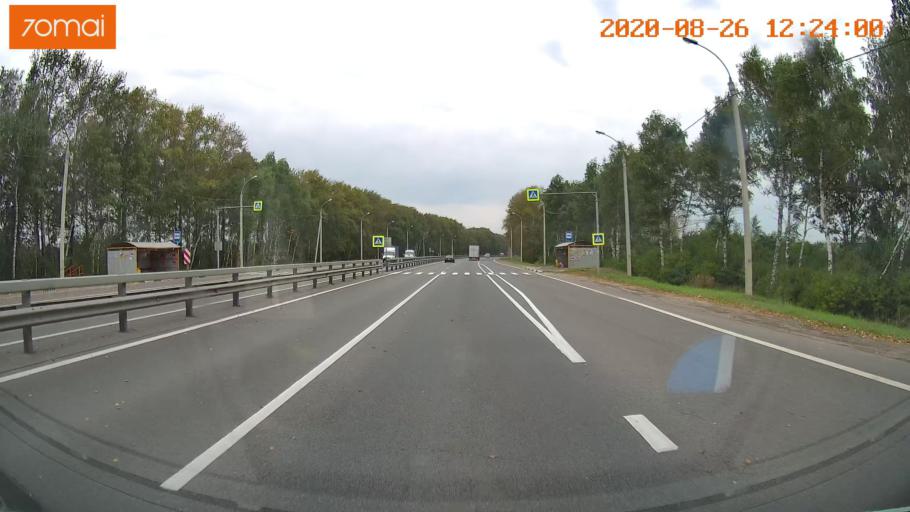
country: RU
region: Rjazan
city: Murmino
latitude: 54.5093
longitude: 39.9002
